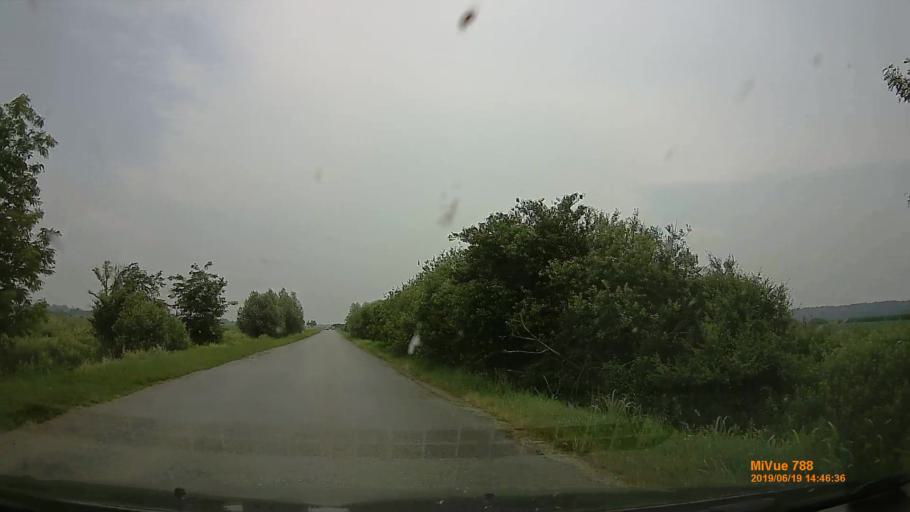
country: HU
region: Baranya
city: Szigetvar
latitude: 46.0047
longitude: 17.8250
